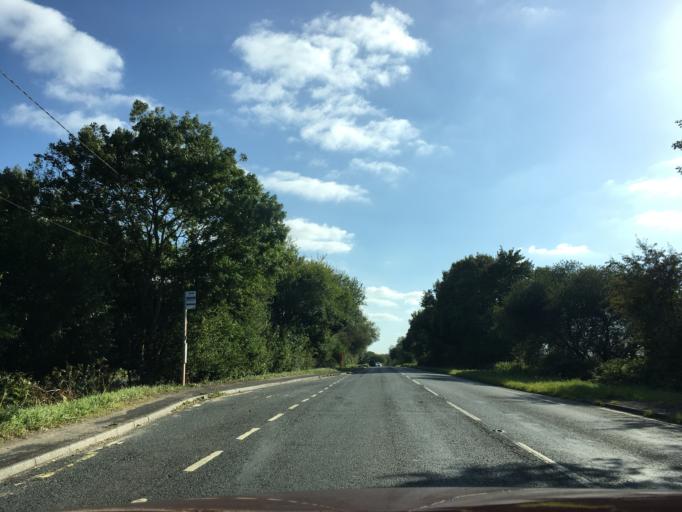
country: GB
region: England
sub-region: Hampshire
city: Tadley
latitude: 51.3385
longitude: -1.1279
